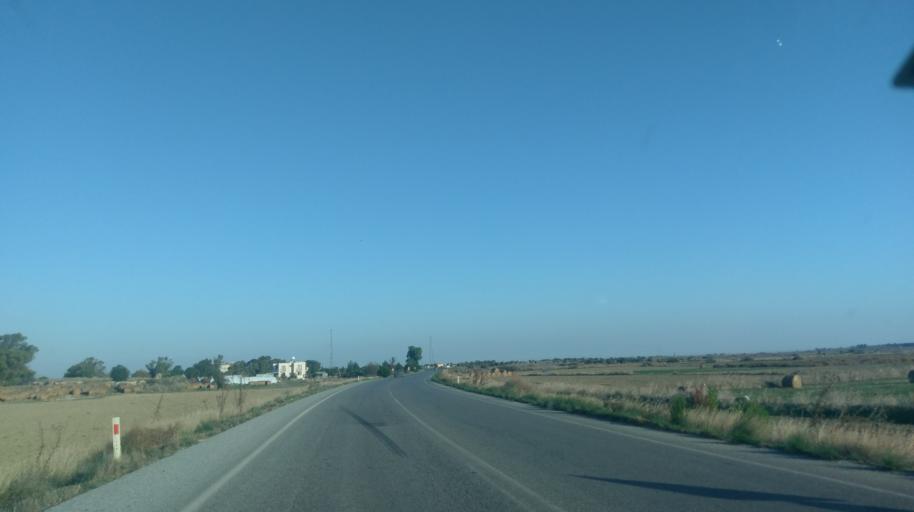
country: CY
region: Ammochostos
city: Lefkonoiko
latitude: 35.2600
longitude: 33.6539
